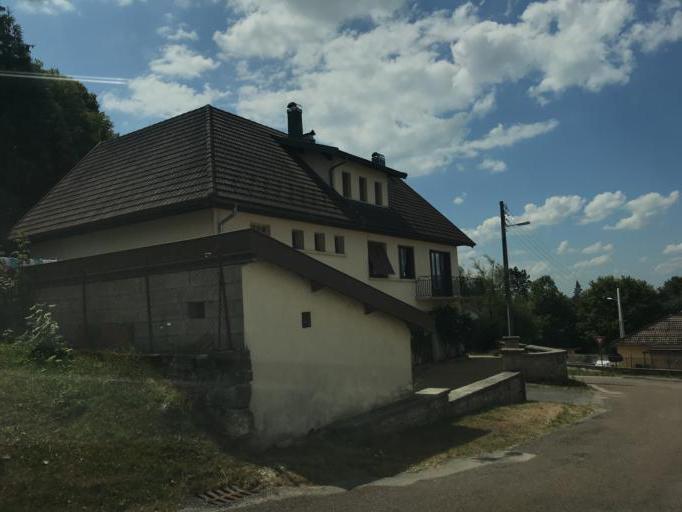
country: FR
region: Franche-Comte
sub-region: Departement du Jura
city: Clairvaux-les-Lacs
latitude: 46.5707
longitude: 5.7574
